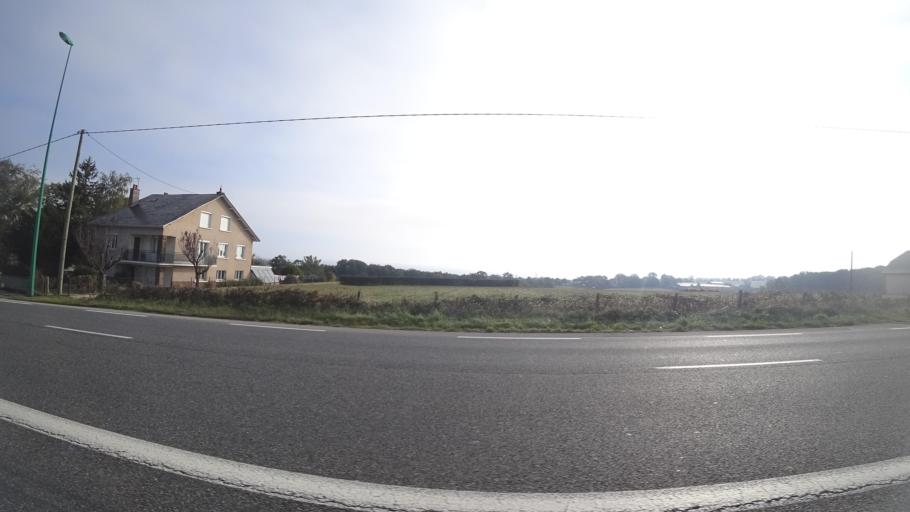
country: FR
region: Midi-Pyrenees
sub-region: Departement de l'Aveyron
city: Luc-la-Primaube
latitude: 44.3037
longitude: 2.5570
